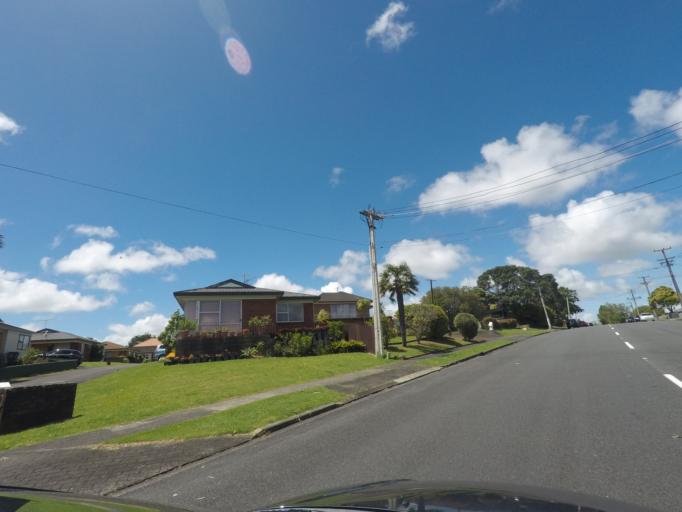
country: NZ
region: Auckland
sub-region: Auckland
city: Rosebank
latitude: -36.8832
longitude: 174.6432
